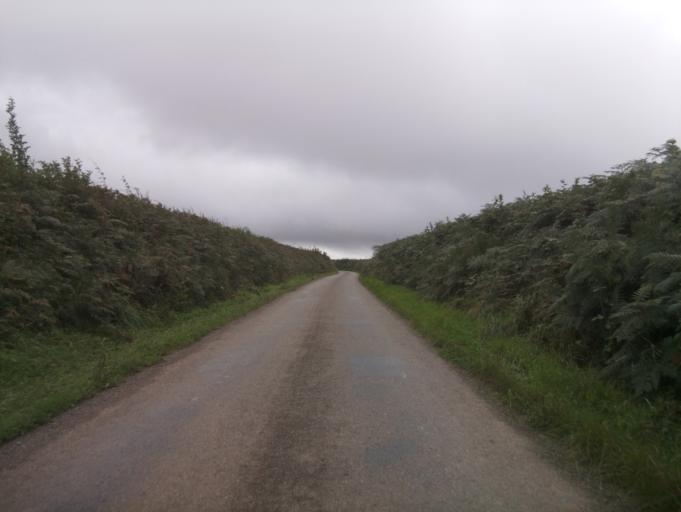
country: GB
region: England
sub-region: Devon
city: Kingsbridge
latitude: 50.3021
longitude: -3.7172
